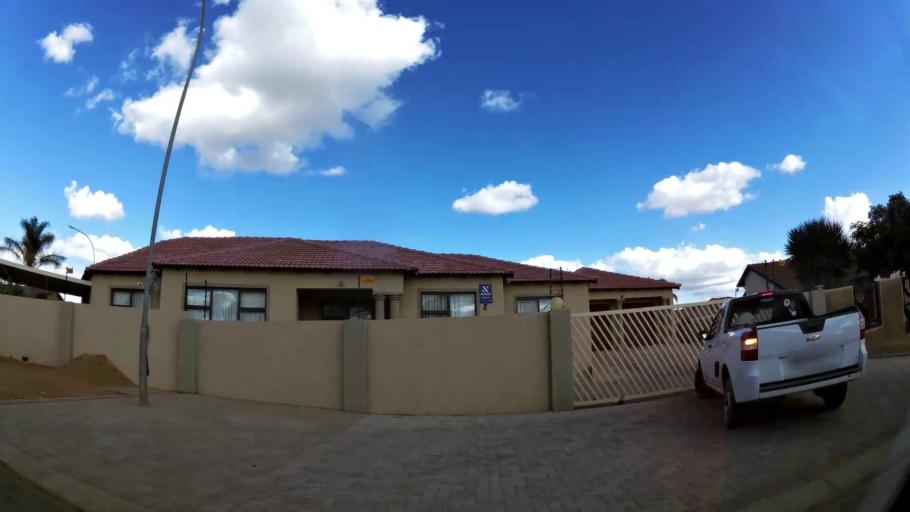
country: ZA
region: Limpopo
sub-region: Capricorn District Municipality
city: Polokwane
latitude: -23.9104
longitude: 29.4995
